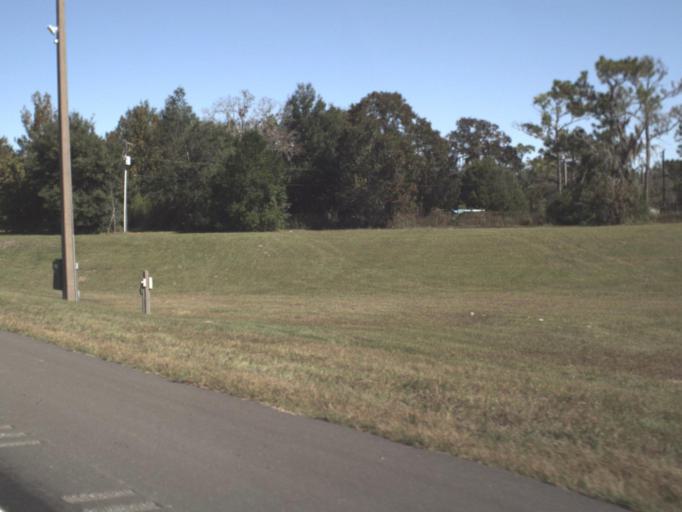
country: US
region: Florida
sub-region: Hernando County
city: Brookridge
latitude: 28.5076
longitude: -82.4767
